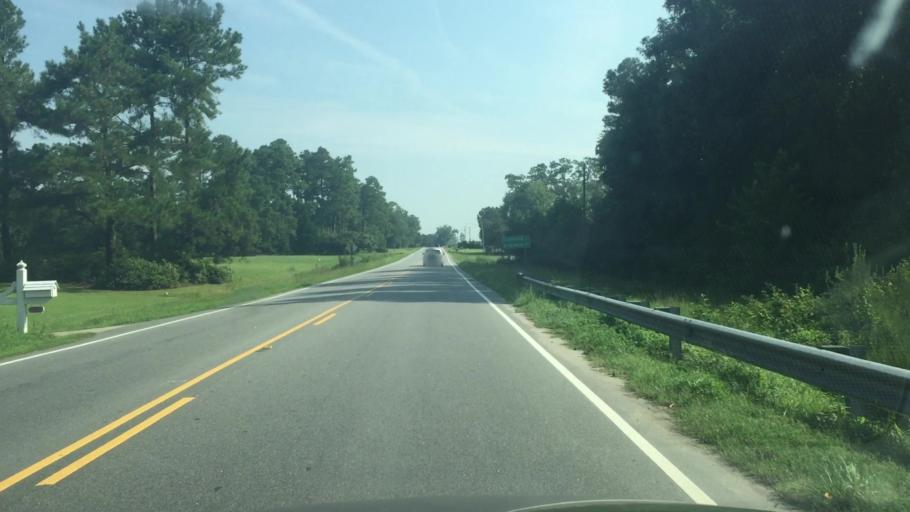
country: US
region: North Carolina
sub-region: Columbus County
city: Tabor City
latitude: 34.1619
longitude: -78.8463
